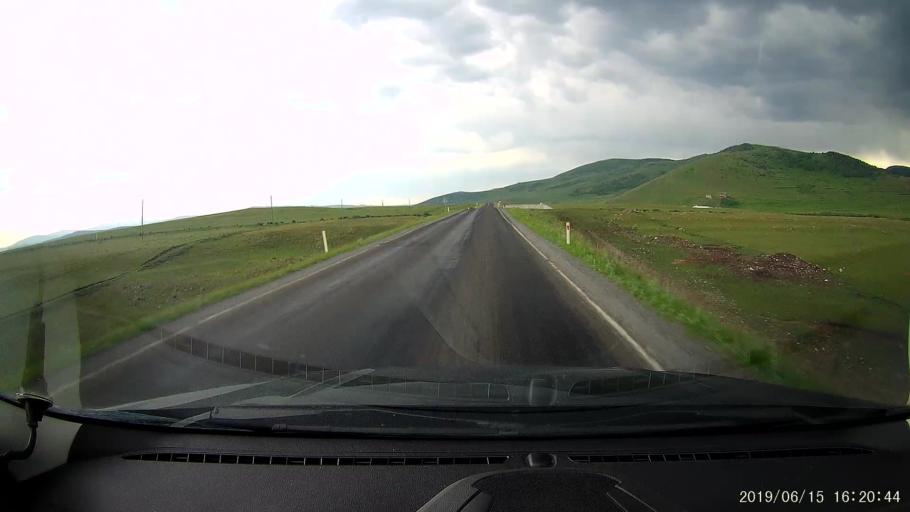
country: TR
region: Ardahan
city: Hanak
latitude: 41.2092
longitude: 42.8466
